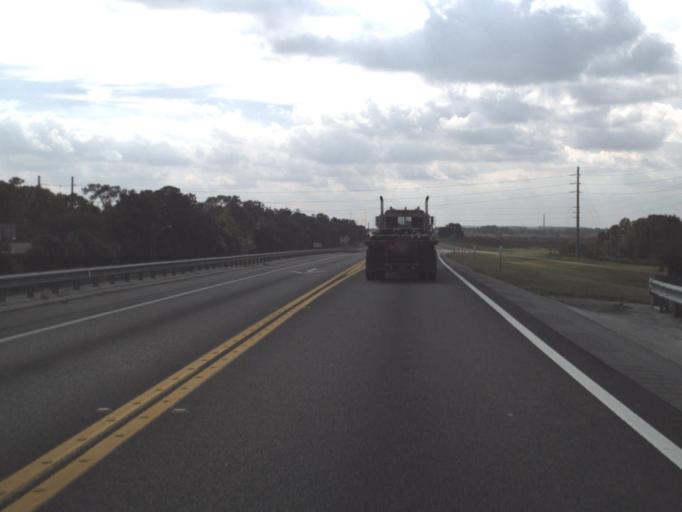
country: US
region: Florida
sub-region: Polk County
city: Fussels Corner
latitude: 28.0729
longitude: -81.8326
